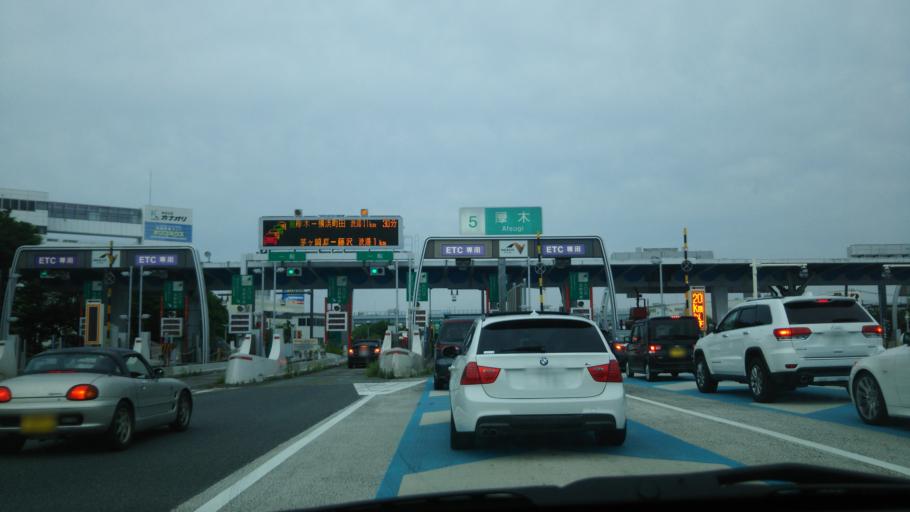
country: JP
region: Kanagawa
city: Atsugi
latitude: 35.4208
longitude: 139.3622
